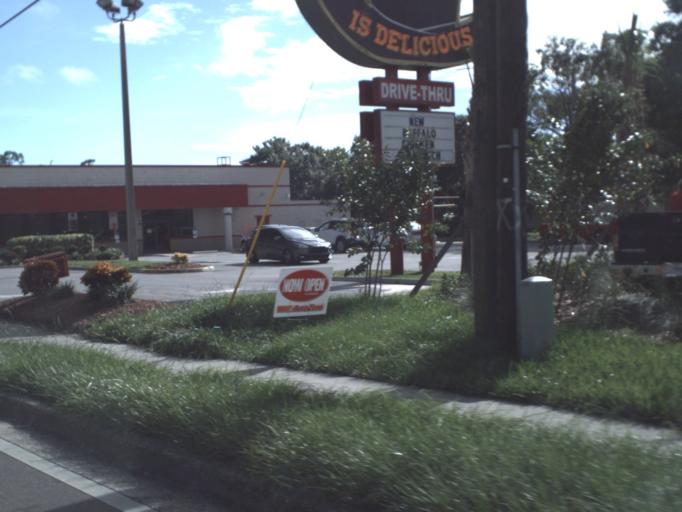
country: US
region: Florida
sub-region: Manatee County
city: West Samoset
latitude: 27.4689
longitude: -82.5630
